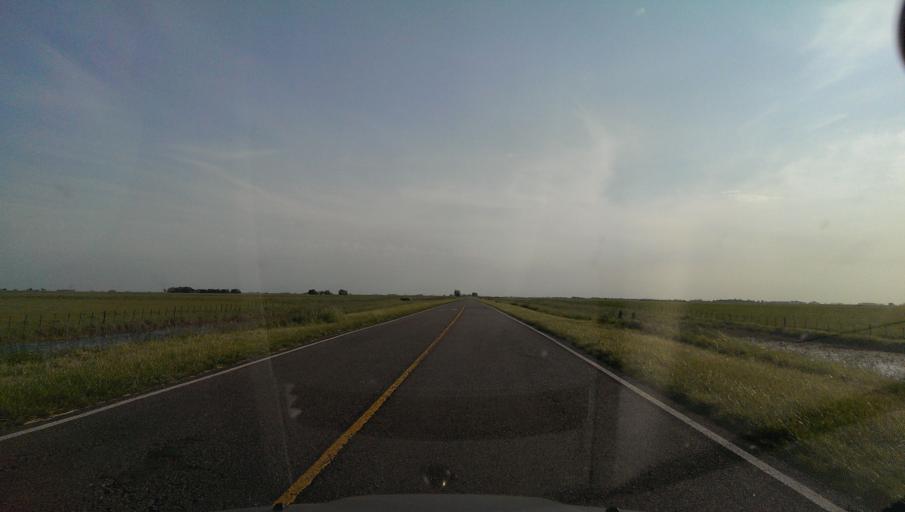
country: AR
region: Buenos Aires
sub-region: Partido de General La Madrid
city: General La Madrid
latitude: -37.4944
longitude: -61.2036
